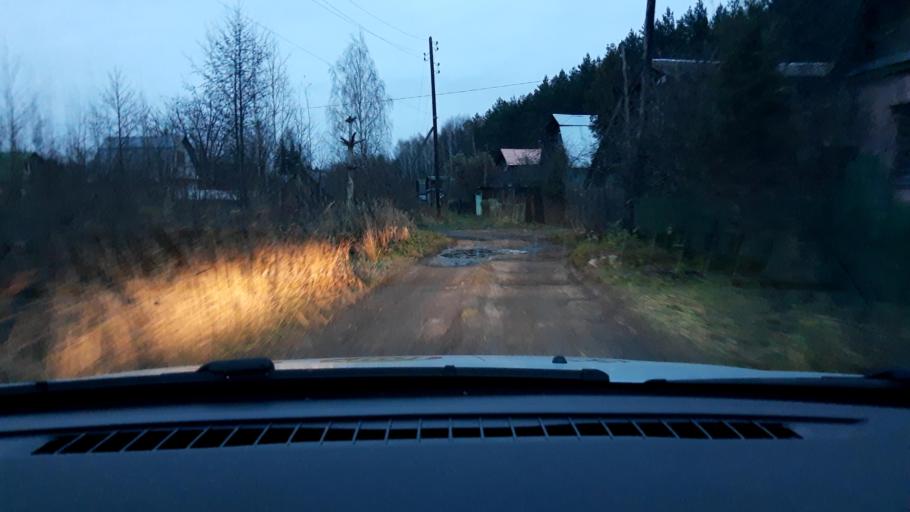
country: RU
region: Nizjnij Novgorod
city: Neklyudovo
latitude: 56.4273
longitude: 44.0094
